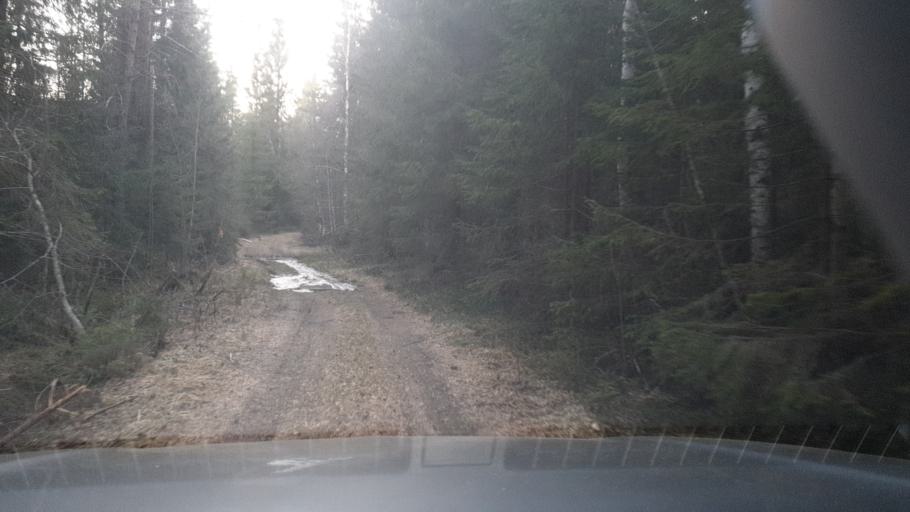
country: SE
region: Vaesternorrland
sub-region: Ange Kommun
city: Ange
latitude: 62.1859
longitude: 15.6188
